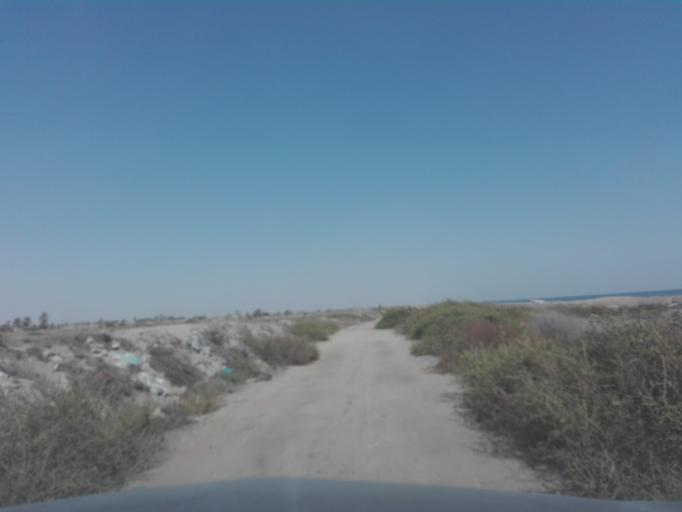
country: TN
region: Qabis
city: Gabes
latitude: 33.9657
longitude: 10.0642
